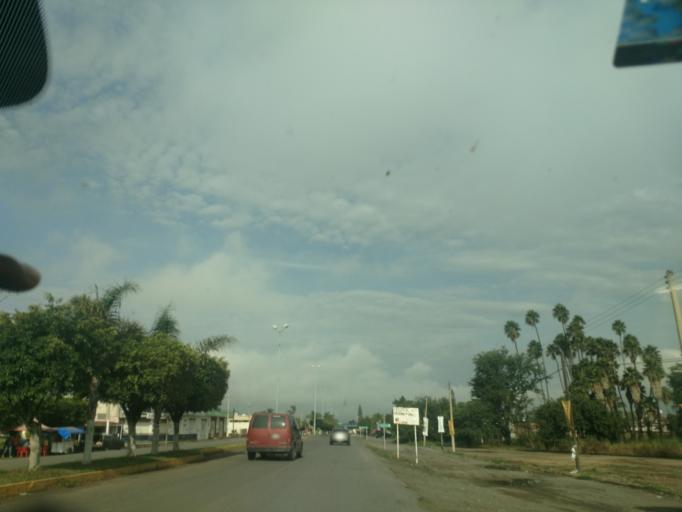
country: MX
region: Jalisco
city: Ameca
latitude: 20.5372
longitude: -104.0377
